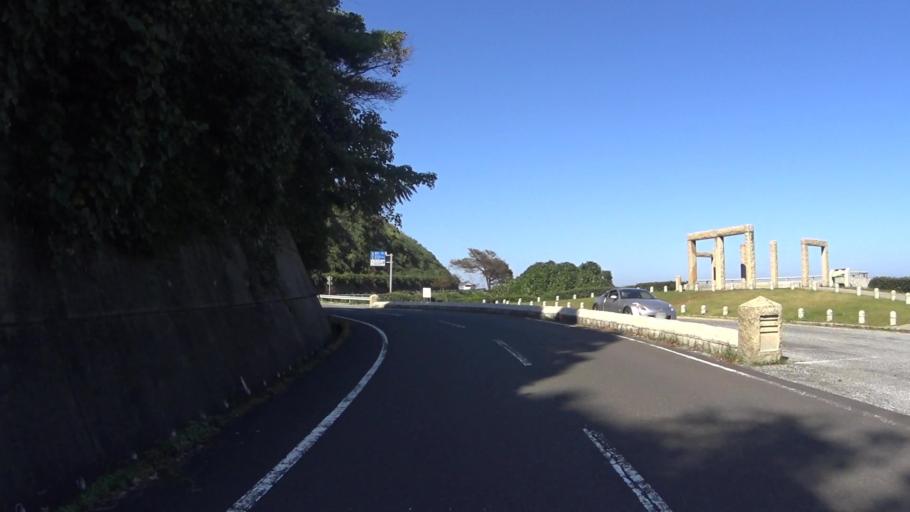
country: JP
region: Kyoto
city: Miyazu
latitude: 35.7571
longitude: 135.2456
